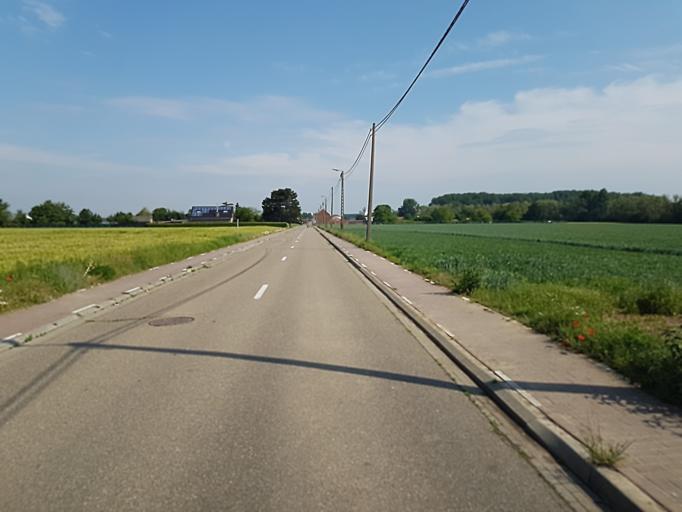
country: BE
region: Flanders
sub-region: Provincie Vlaams-Brabant
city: Leuven
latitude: 50.9074
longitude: 4.6994
